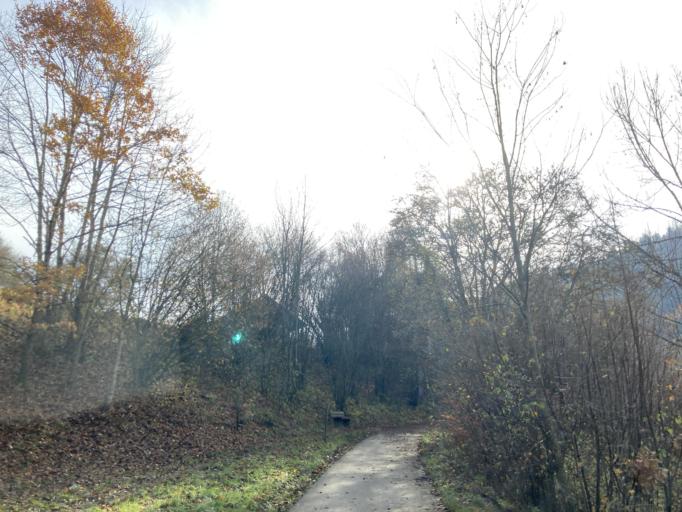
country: DE
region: Baden-Wuerttemberg
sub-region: Tuebingen Region
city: Hirrlingen
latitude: 48.4608
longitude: 8.8646
